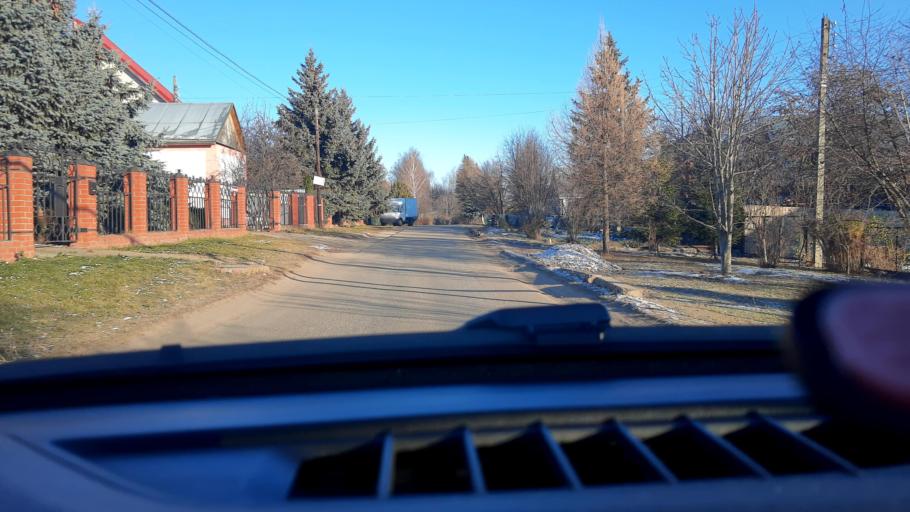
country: RU
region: Nizjnij Novgorod
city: Burevestnik
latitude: 56.2007
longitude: 43.8777
